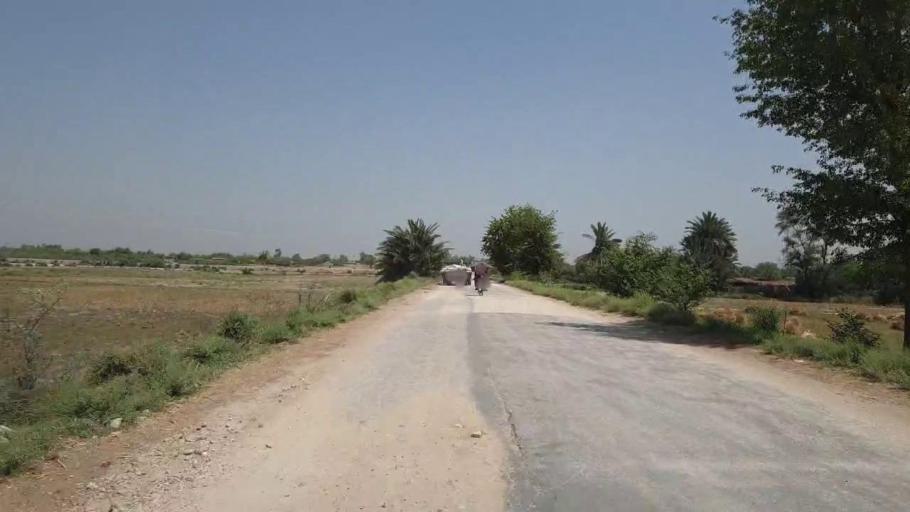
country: PK
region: Sindh
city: Adilpur
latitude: 27.8895
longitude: 69.2888
